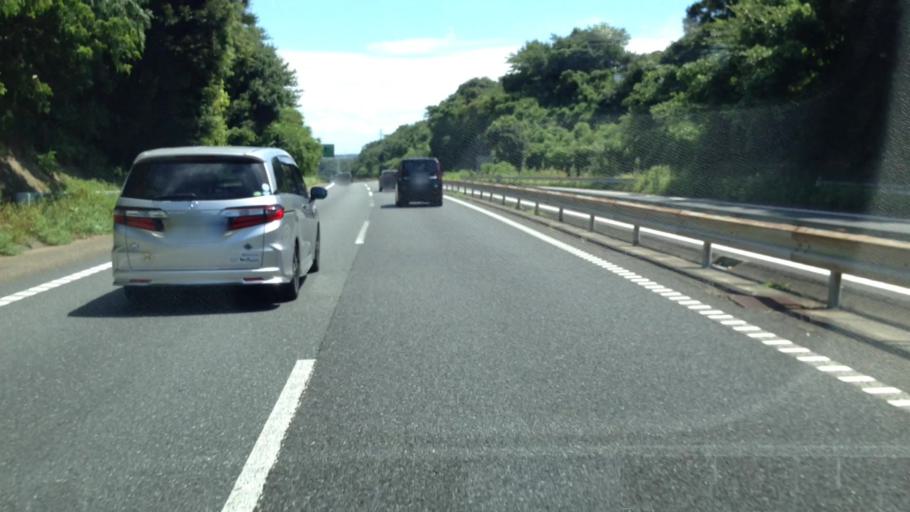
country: JP
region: Kanagawa
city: Yokosuka
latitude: 35.2475
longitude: 139.6469
